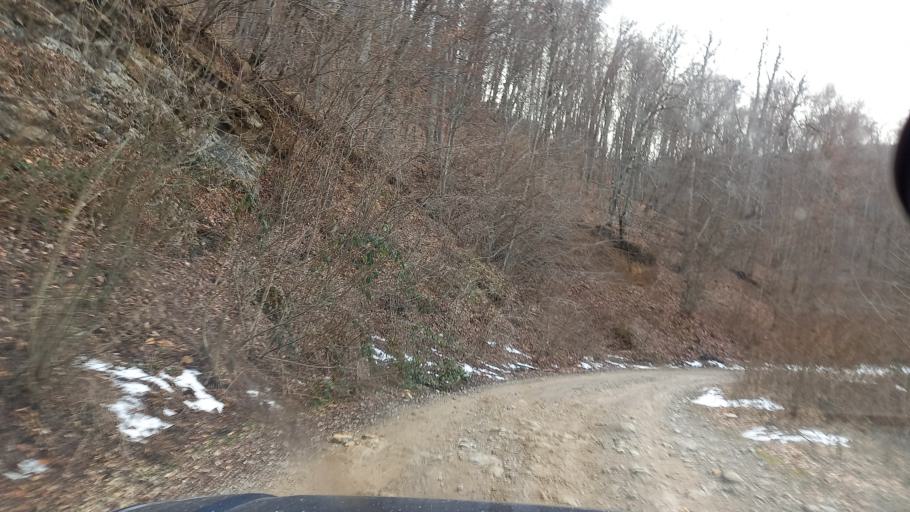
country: RU
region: Adygeya
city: Kamennomostskiy
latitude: 44.1646
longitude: 40.3009
